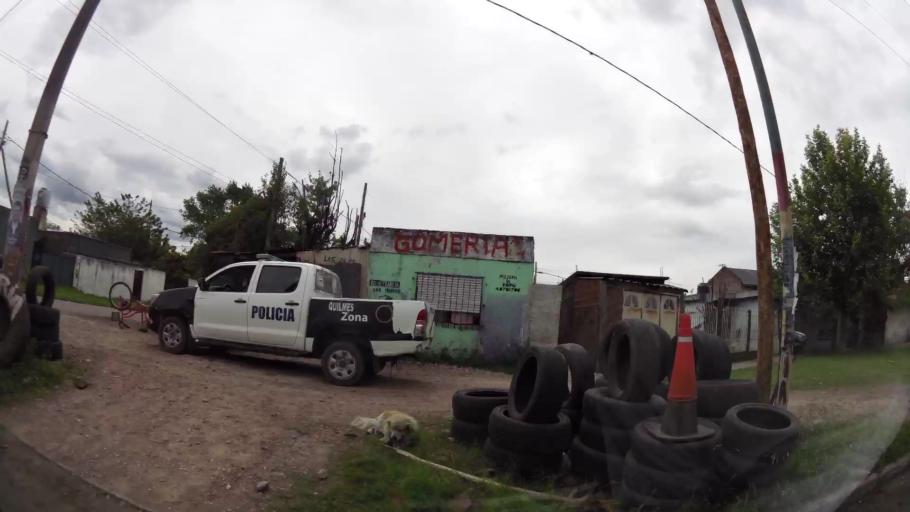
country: AR
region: Buenos Aires
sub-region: Partido de Quilmes
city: Quilmes
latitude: -34.7631
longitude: -58.2617
